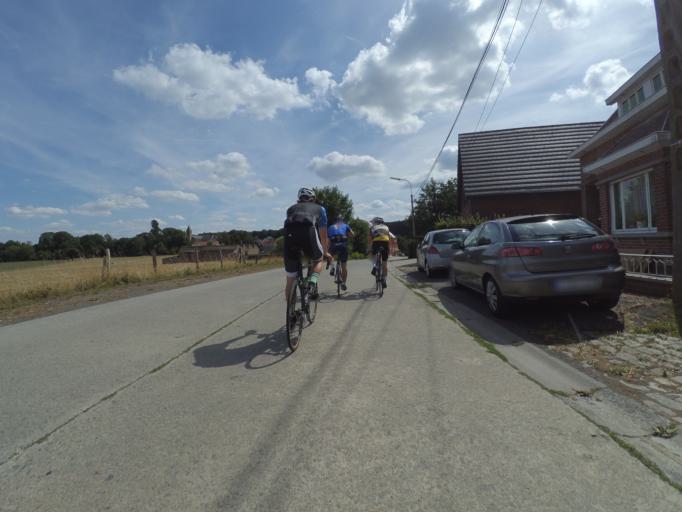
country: BE
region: Flanders
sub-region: Provincie Oost-Vlaanderen
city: Ronse
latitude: 50.7735
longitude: 3.6386
